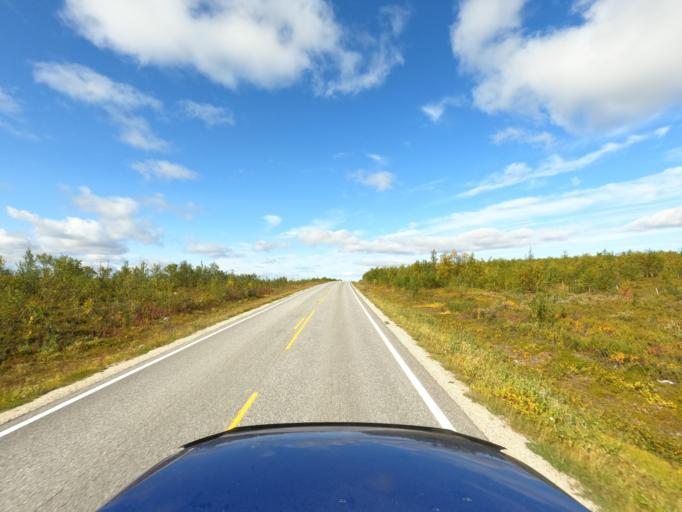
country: NO
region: Finnmark Fylke
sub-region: Karasjok
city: Karasjohka
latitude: 69.5539
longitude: 25.4049
